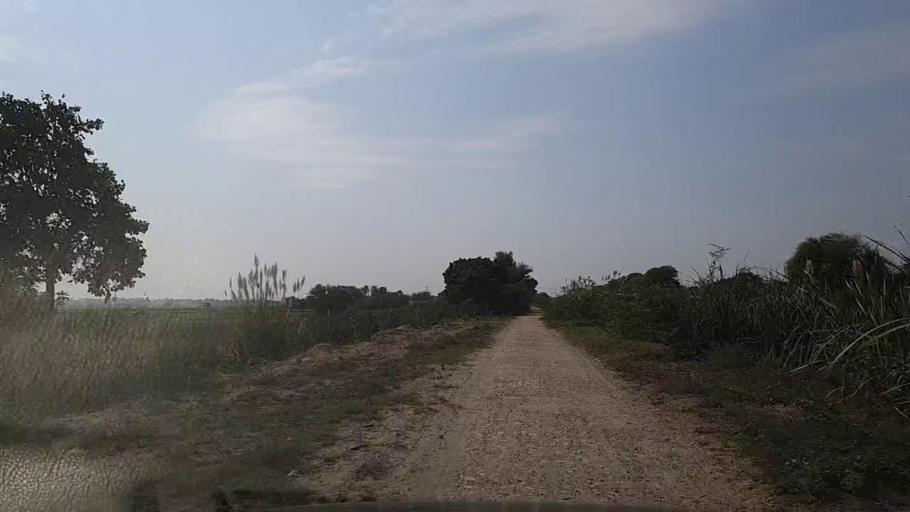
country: PK
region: Sindh
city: Thatta
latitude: 24.7640
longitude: 67.7879
